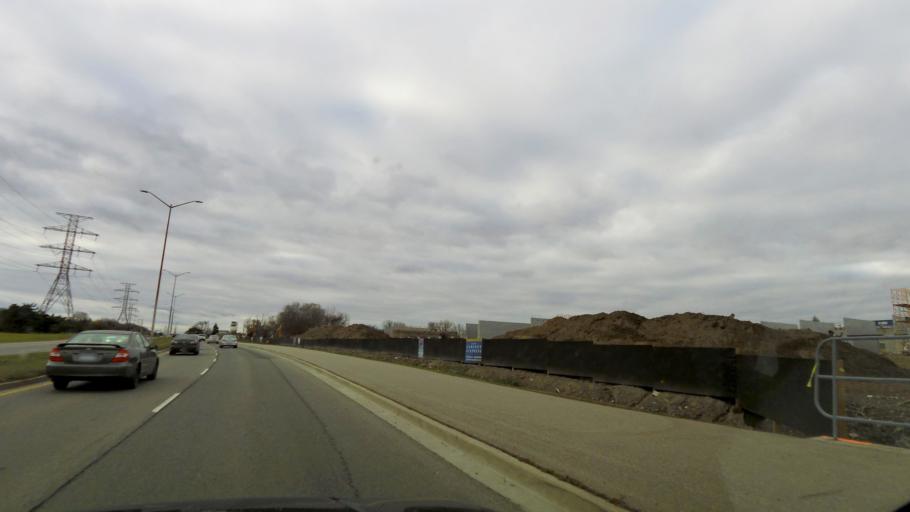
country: CA
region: Ontario
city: Etobicoke
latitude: 43.6003
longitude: -79.5786
